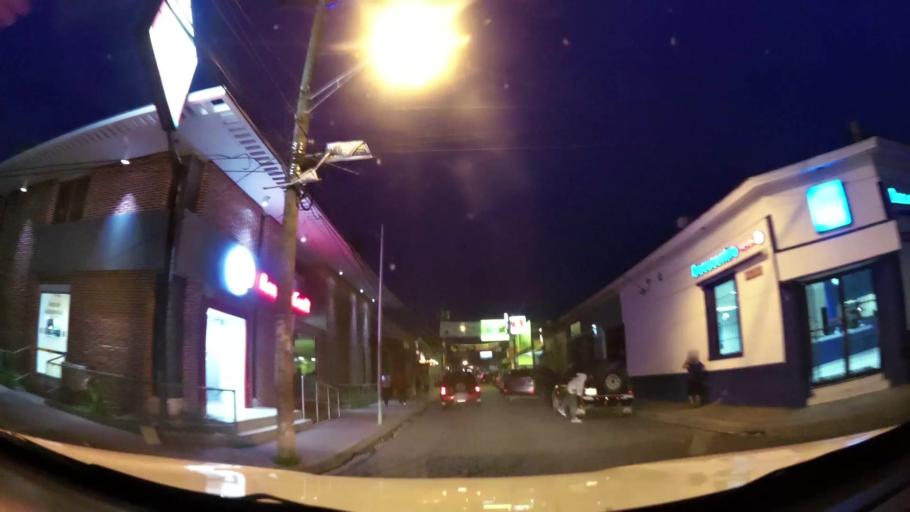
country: NI
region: Esteli
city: Esteli
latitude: 13.0915
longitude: -86.3575
